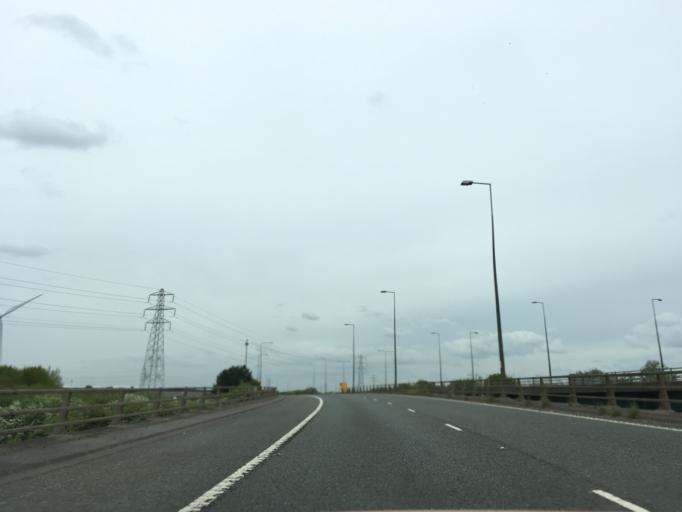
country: GB
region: England
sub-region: North Somerset
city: Easton-in-Gordano
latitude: 51.5061
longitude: -2.6692
